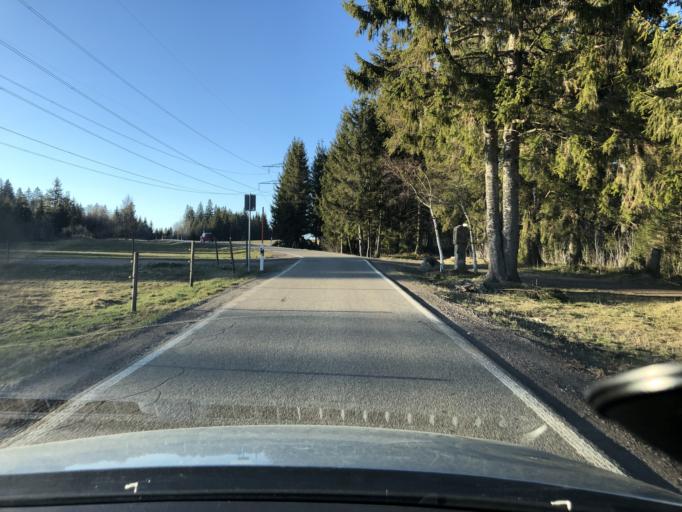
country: DE
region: Baden-Wuerttemberg
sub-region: Freiburg Region
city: Schluchsee
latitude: 47.8158
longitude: 8.2129
